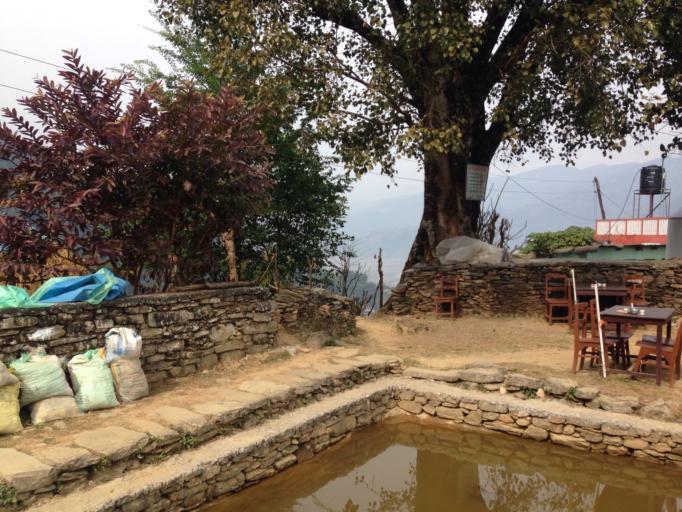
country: NP
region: Western Region
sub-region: Gandaki Zone
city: Pokhara
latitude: 28.2056
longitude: 83.9458
